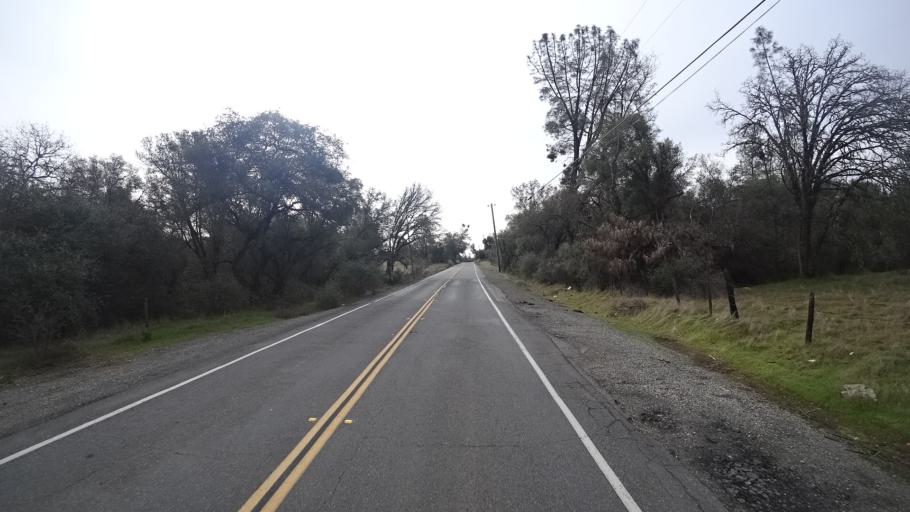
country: US
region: California
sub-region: Butte County
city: Oroville East
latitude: 39.4407
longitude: -121.4316
